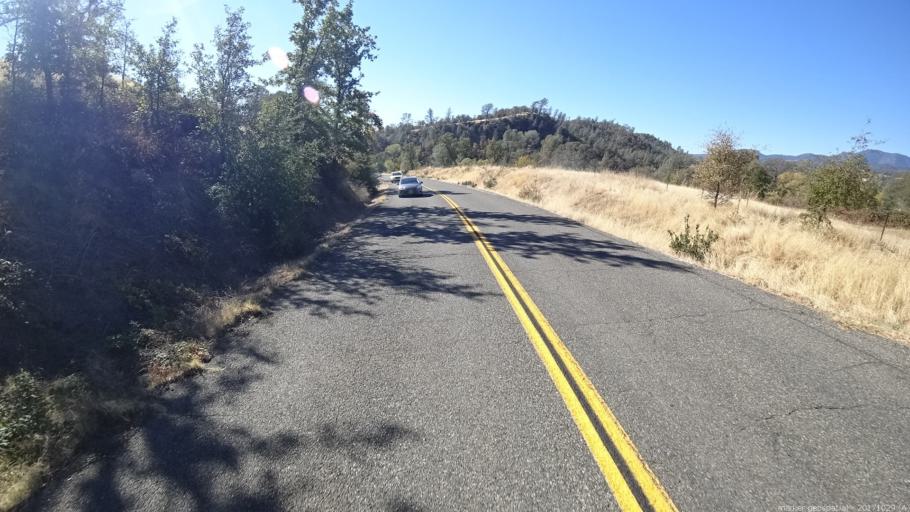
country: US
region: California
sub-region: Shasta County
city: Shasta
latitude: 40.4732
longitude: -122.6209
